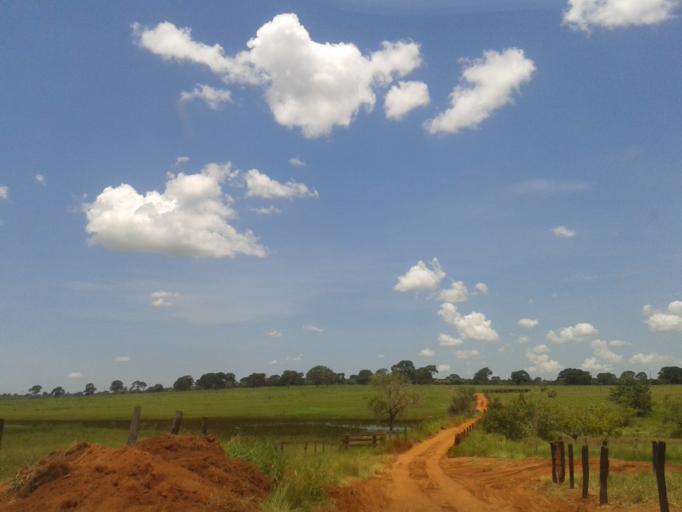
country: BR
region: Minas Gerais
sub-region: Santa Vitoria
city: Santa Vitoria
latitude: -19.2107
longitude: -50.4040
